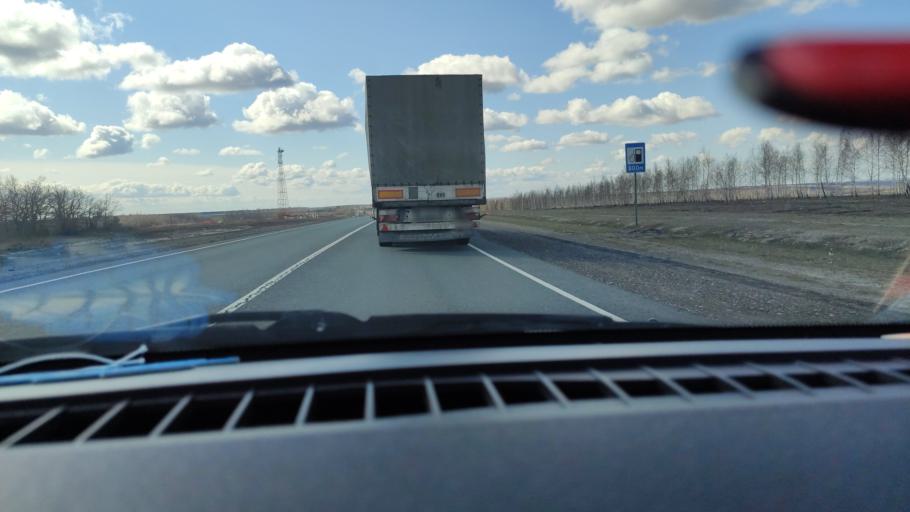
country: RU
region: Samara
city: Syzran'
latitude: 52.9285
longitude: 48.3055
